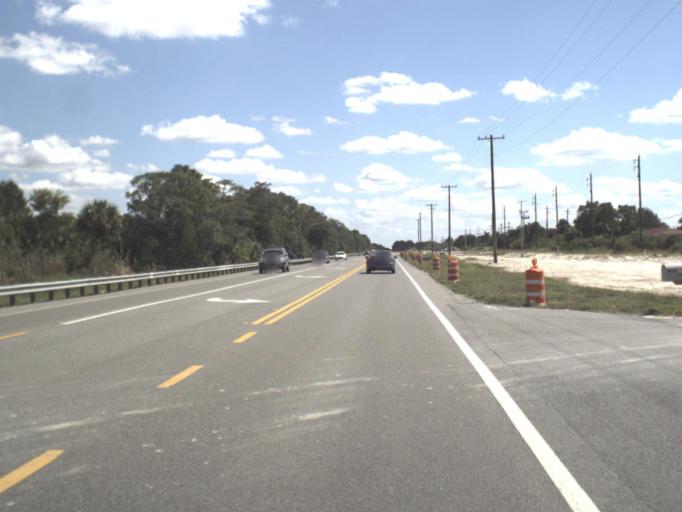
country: US
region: Florida
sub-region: Collier County
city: Lely Resort
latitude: 26.0381
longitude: -81.6597
